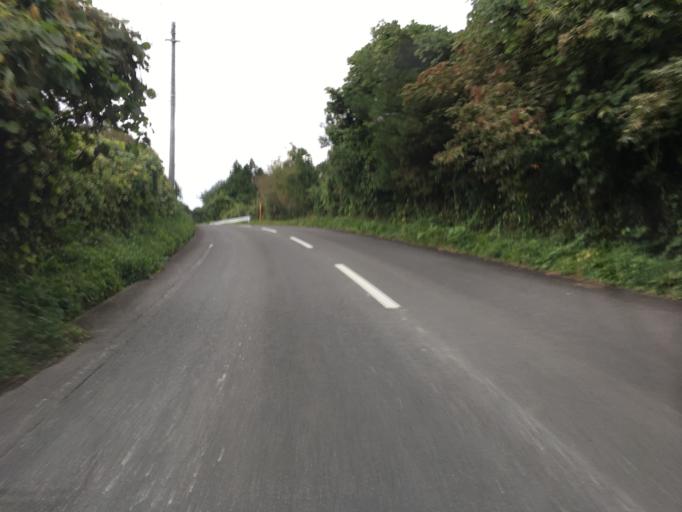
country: JP
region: Fukushima
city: Fukushima-shi
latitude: 37.6566
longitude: 140.5716
